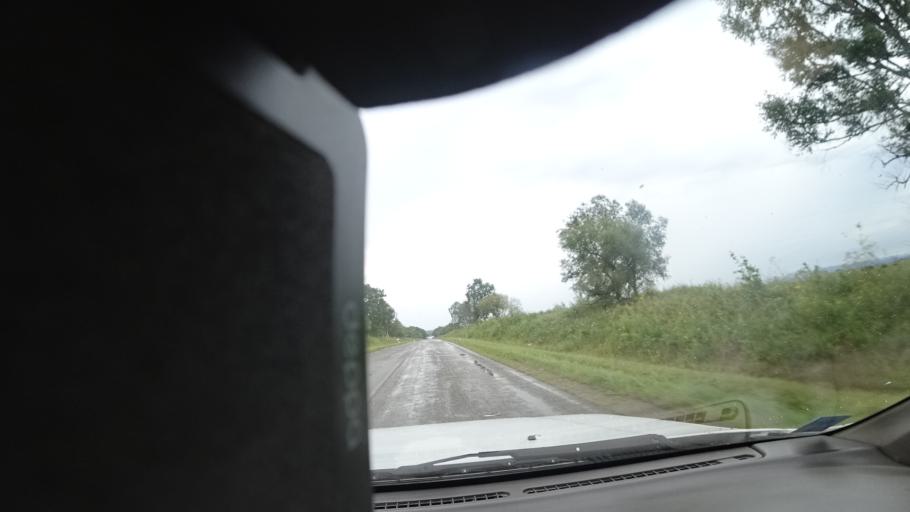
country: RU
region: Primorskiy
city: Lazo
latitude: 45.8701
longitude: 133.7109
